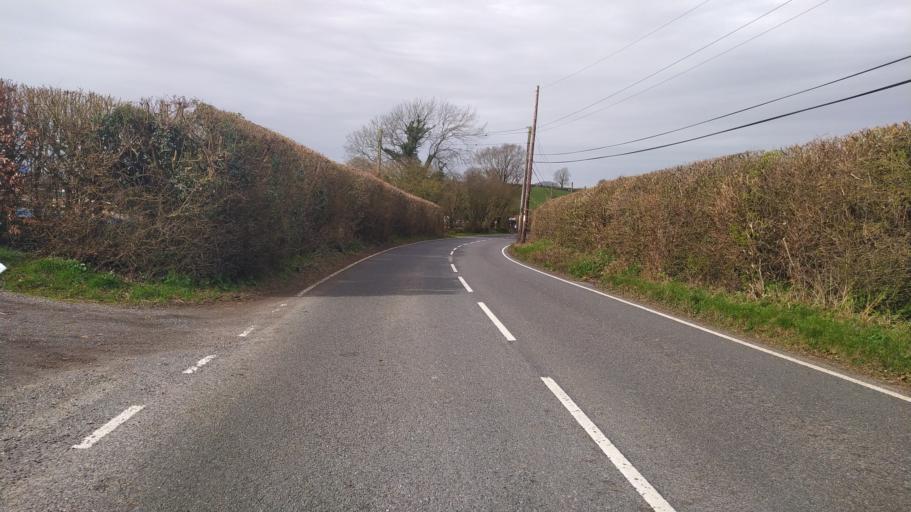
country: GB
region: England
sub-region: Dorset
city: Beaminster
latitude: 50.8576
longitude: -2.7367
